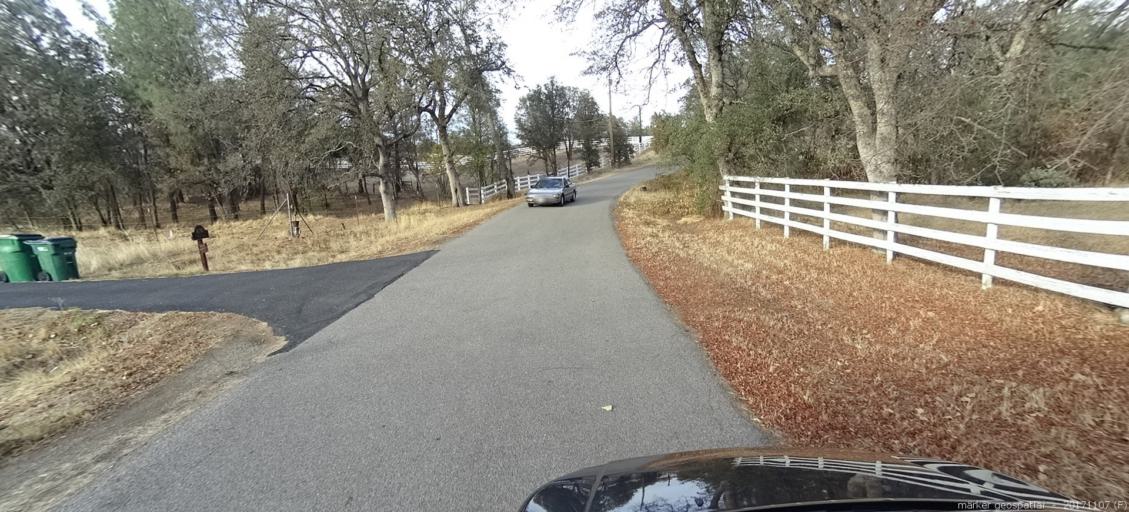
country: US
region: California
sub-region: Shasta County
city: Shasta
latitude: 40.5232
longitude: -122.4783
